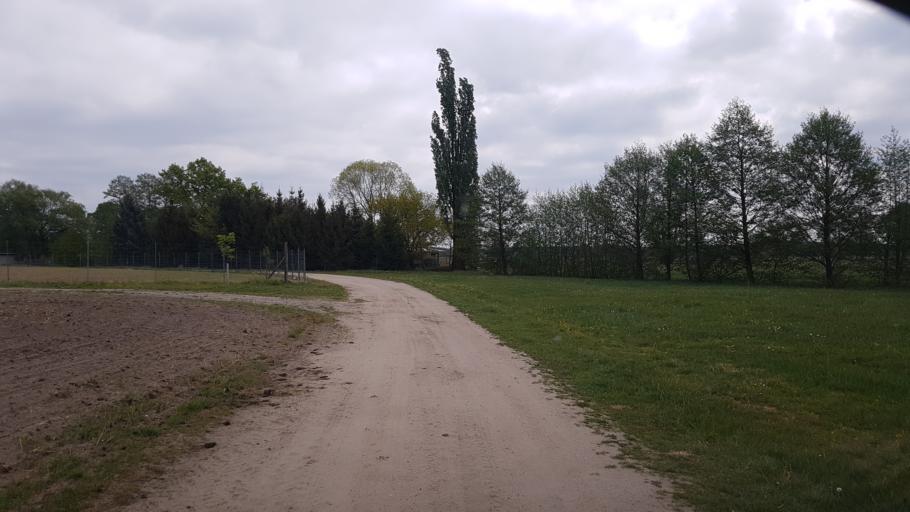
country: DE
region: Brandenburg
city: Schonewalde
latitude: 51.6671
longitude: 13.6241
